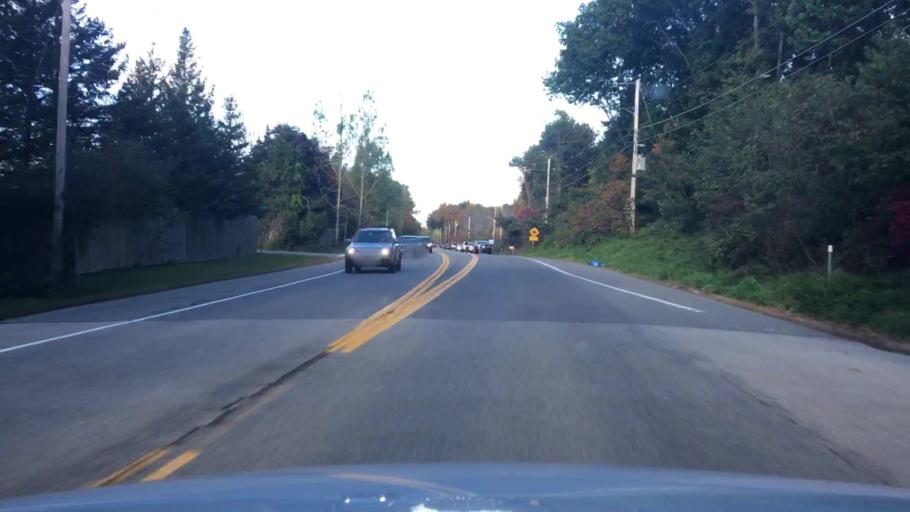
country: US
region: New Hampshire
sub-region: Strafford County
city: Durham
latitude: 43.1352
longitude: -70.8903
